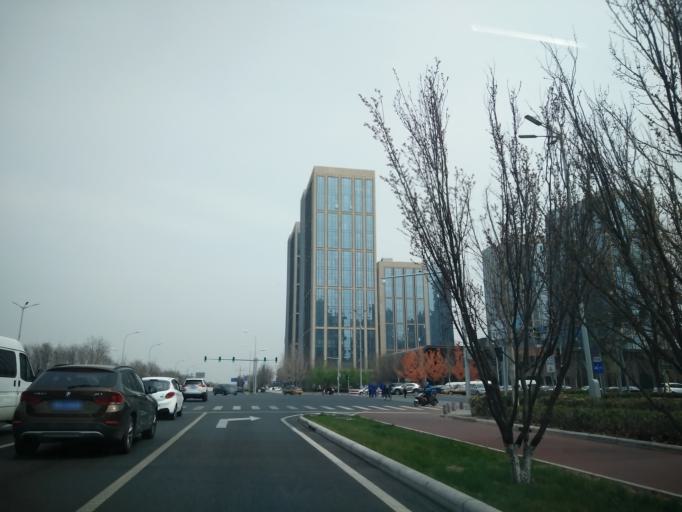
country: CN
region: Beijing
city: Jiugong
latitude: 39.8076
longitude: 116.4902
